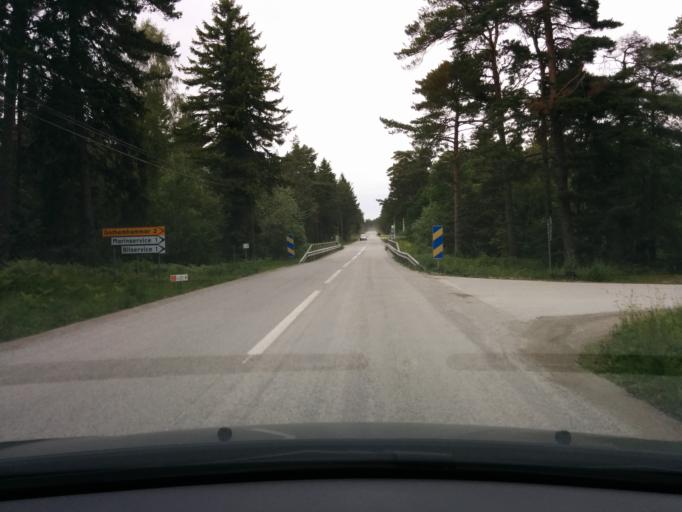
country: SE
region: Gotland
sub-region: Gotland
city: Slite
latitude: 57.6123
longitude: 18.7553
